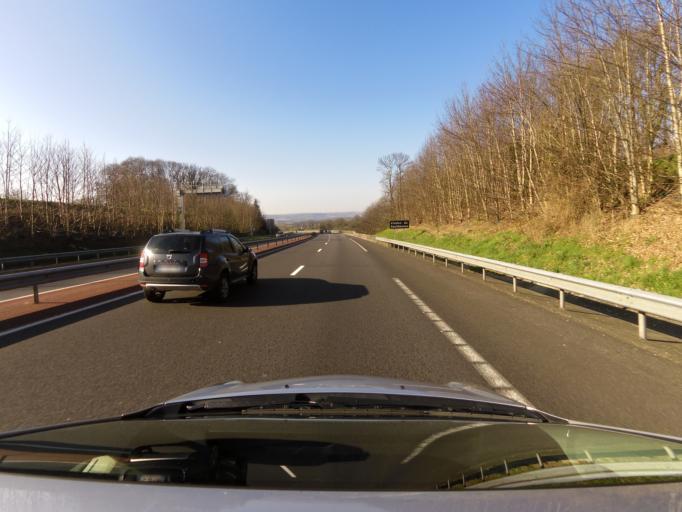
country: FR
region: Lower Normandy
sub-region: Departement de la Manche
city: Saint-Senier-sous-Avranches
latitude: 48.7403
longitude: -1.2920
